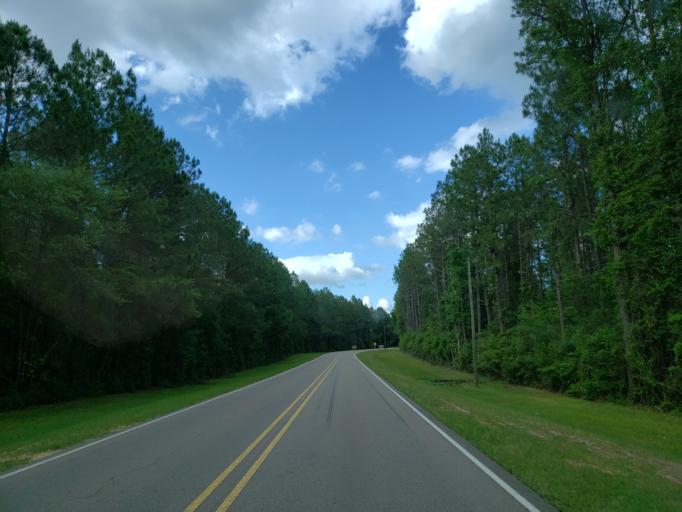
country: US
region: Mississippi
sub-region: Forrest County
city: Petal
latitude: 31.2680
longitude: -89.2124
